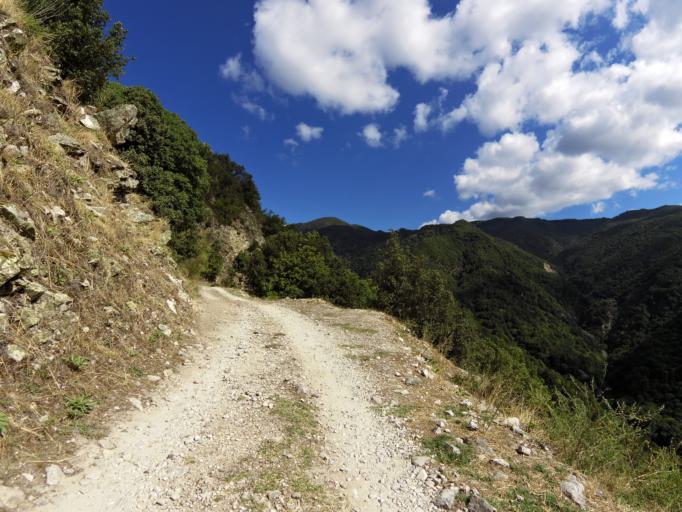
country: IT
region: Calabria
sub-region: Provincia di Reggio Calabria
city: Bivongi
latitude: 38.4911
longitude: 16.4061
